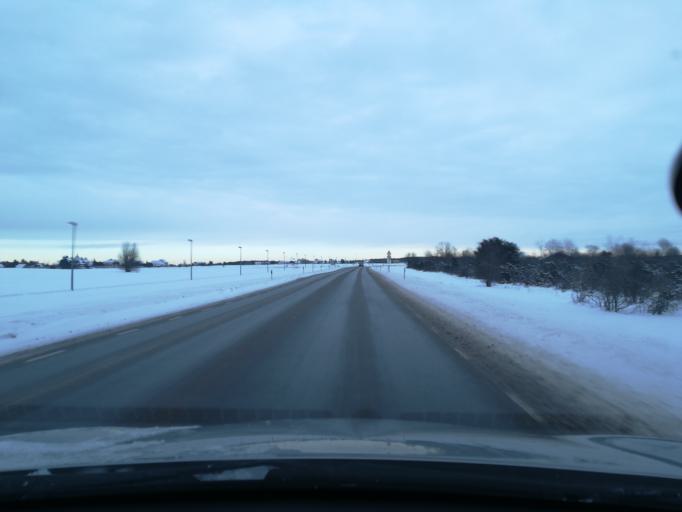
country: EE
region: Harju
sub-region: Harku vald
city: Tabasalu
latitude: 59.4474
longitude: 24.4738
